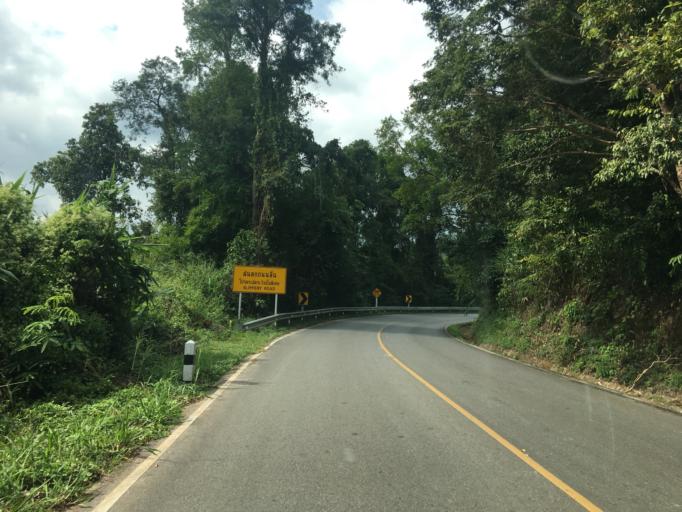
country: TH
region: Nan
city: Ban Luang
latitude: 18.8728
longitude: 100.5460
